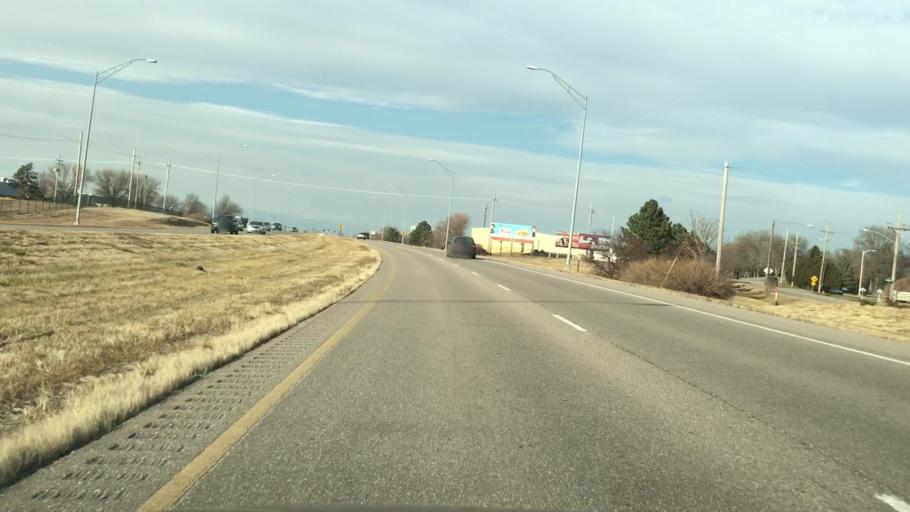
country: US
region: Nebraska
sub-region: Hall County
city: Grand Island
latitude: 40.8971
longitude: -98.3787
